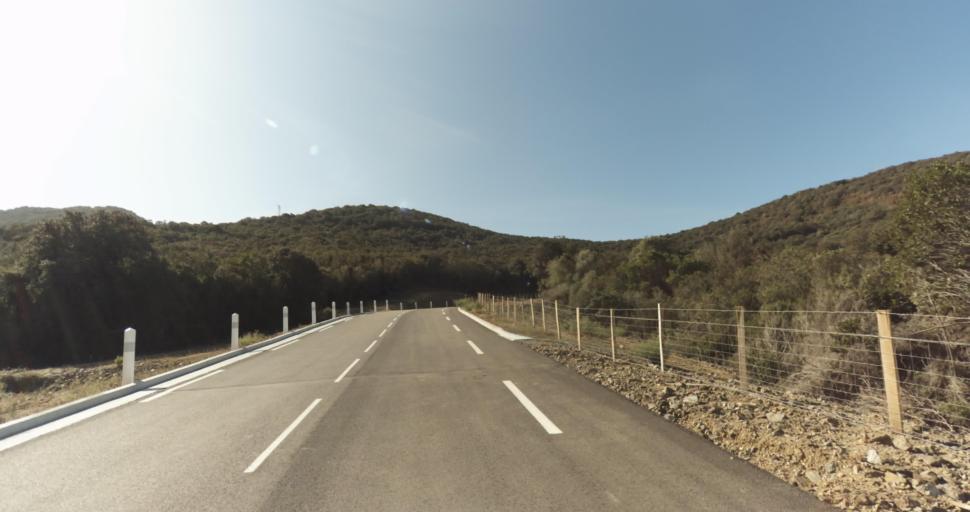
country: FR
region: Corsica
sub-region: Departement de la Corse-du-Sud
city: Ajaccio
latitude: 41.9269
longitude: 8.6490
